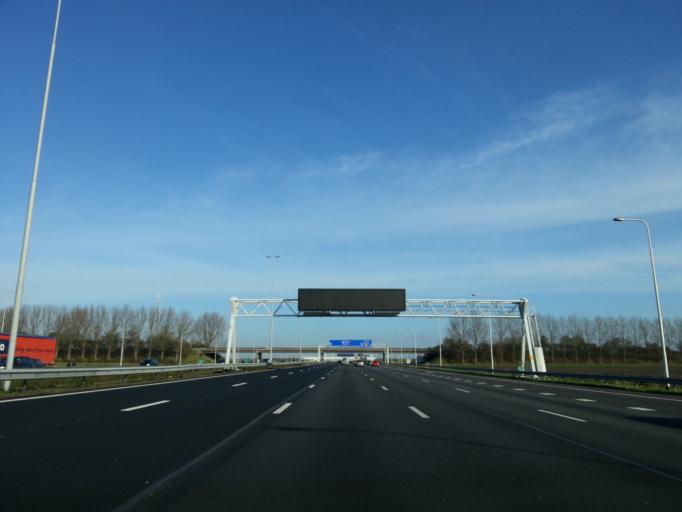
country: NL
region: North Holland
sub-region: Gemeente Haarlemmermeer
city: Hoofddorp
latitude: 52.2650
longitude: 4.6938
